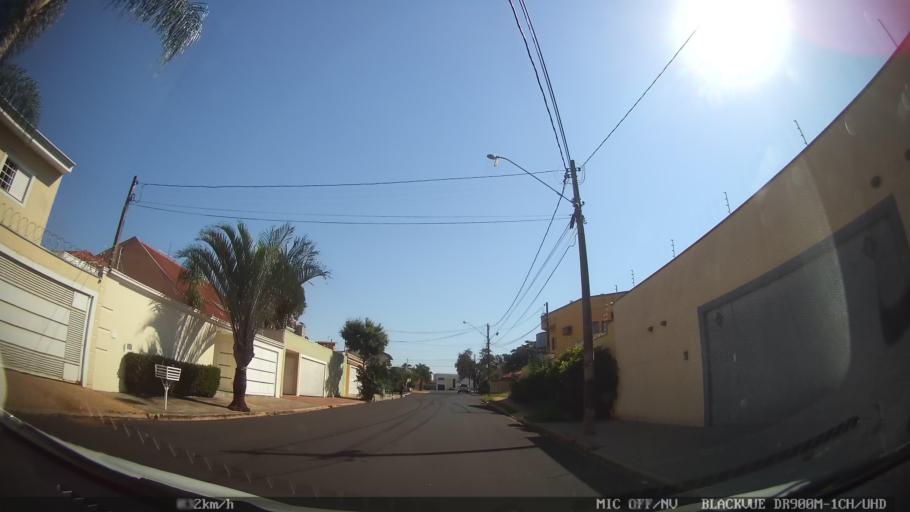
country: BR
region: Sao Paulo
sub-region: Ribeirao Preto
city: Ribeirao Preto
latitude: -21.2028
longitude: -47.7722
